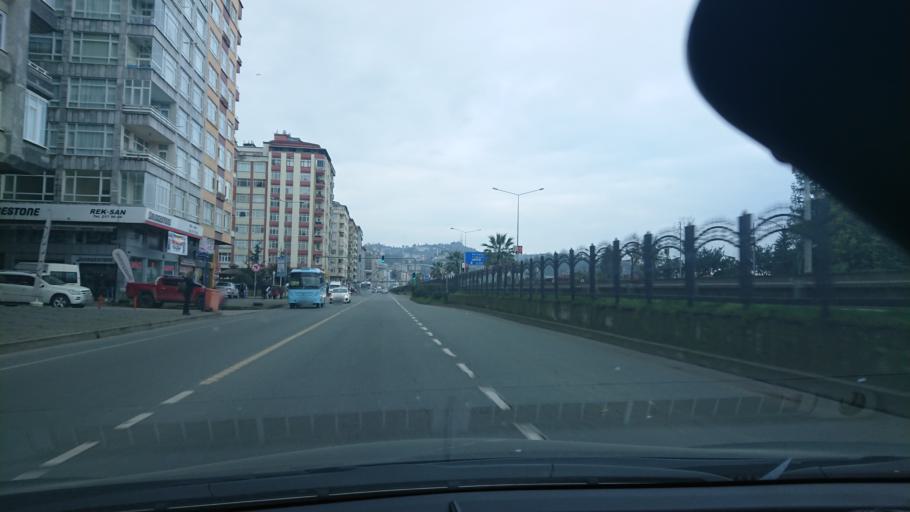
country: TR
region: Rize
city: Rize
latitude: 41.0256
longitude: 40.5301
